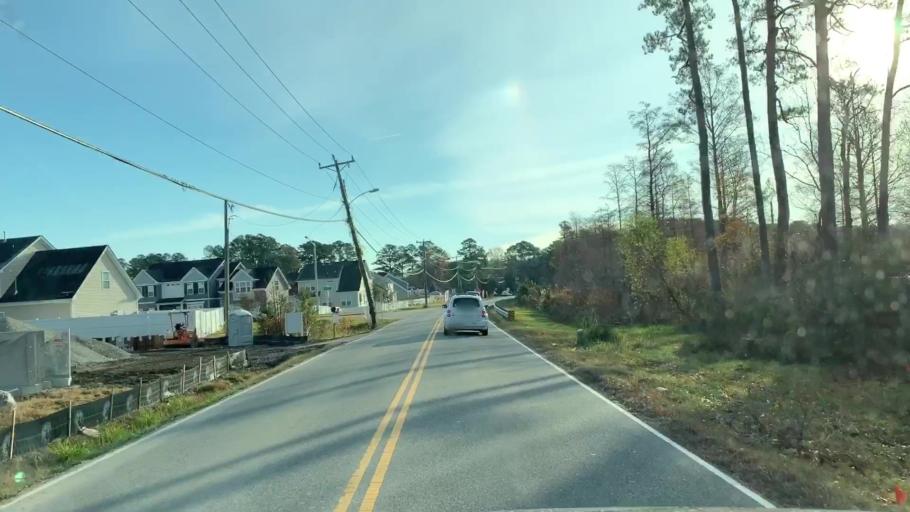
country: US
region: Virginia
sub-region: City of Chesapeake
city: Chesapeake
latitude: 36.7613
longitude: -76.1453
